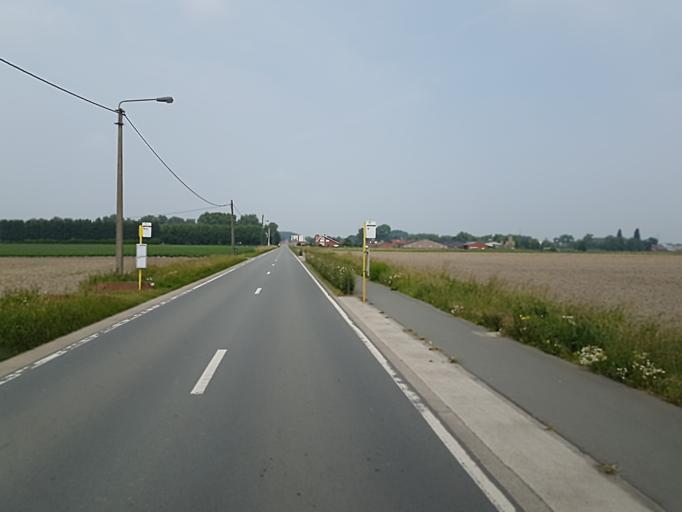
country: BE
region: Flanders
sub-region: Provincie West-Vlaanderen
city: Ardooie
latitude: 50.9500
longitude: 3.2011
